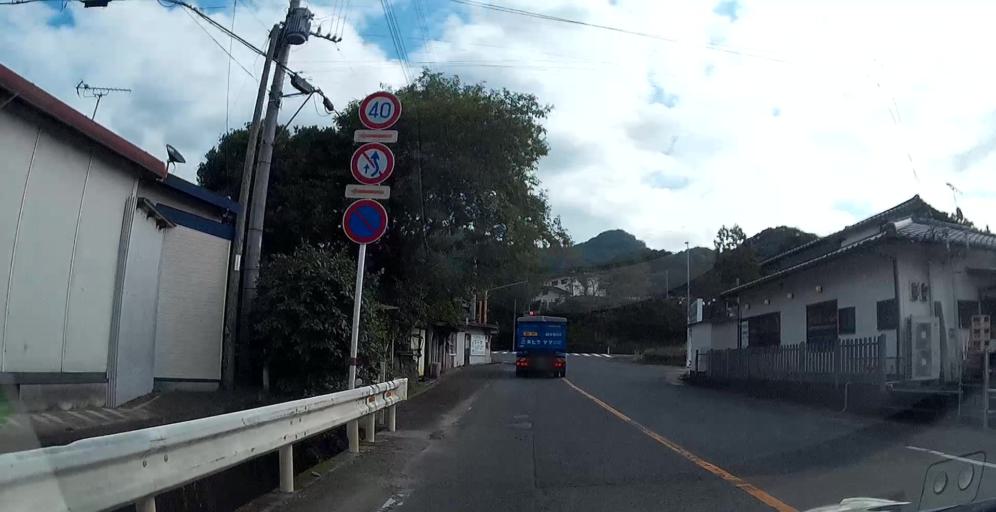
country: JP
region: Kumamoto
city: Minamata
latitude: 32.2267
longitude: 130.4377
